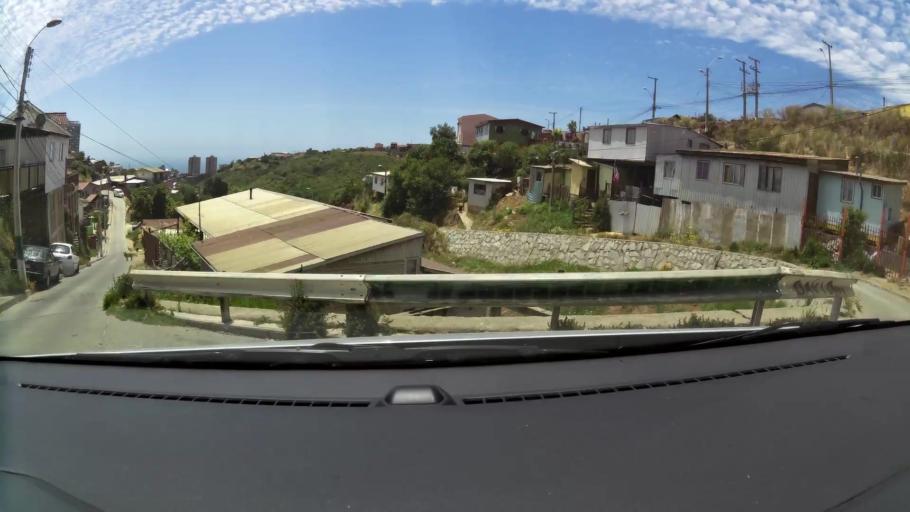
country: CL
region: Valparaiso
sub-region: Provincia de Valparaiso
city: Vina del Mar
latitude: -33.0515
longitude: -71.5714
